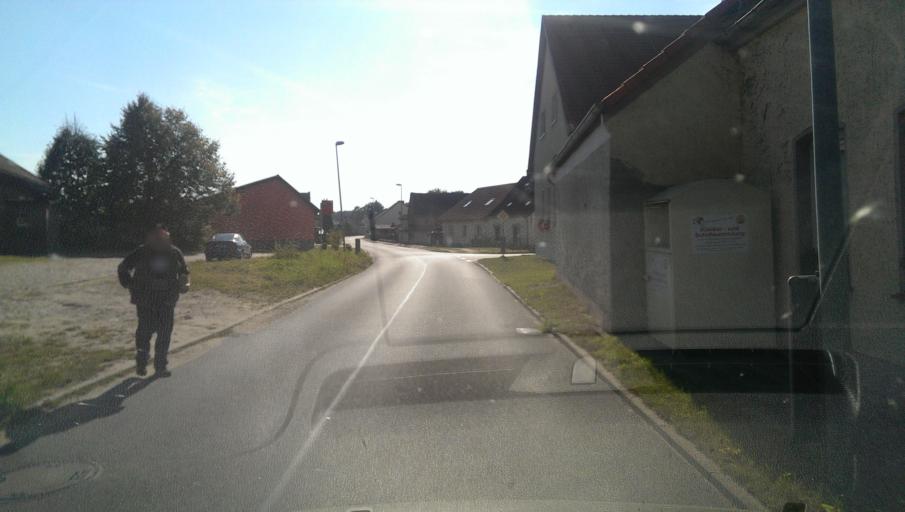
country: DE
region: Brandenburg
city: Halbe
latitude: 52.0752
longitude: 13.7266
